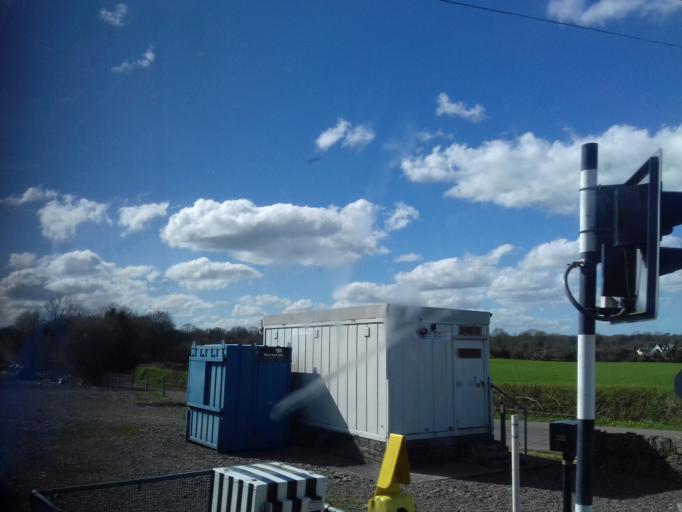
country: IE
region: Munster
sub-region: County Cork
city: Kanturk
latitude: 52.1287
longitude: -8.9012
